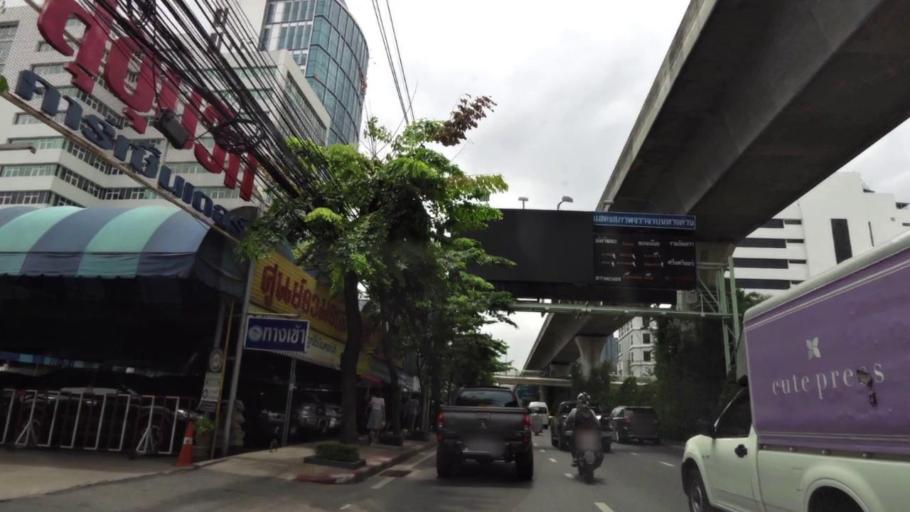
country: TH
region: Bangkok
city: Phra Khanong
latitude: 13.6935
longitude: 100.6067
